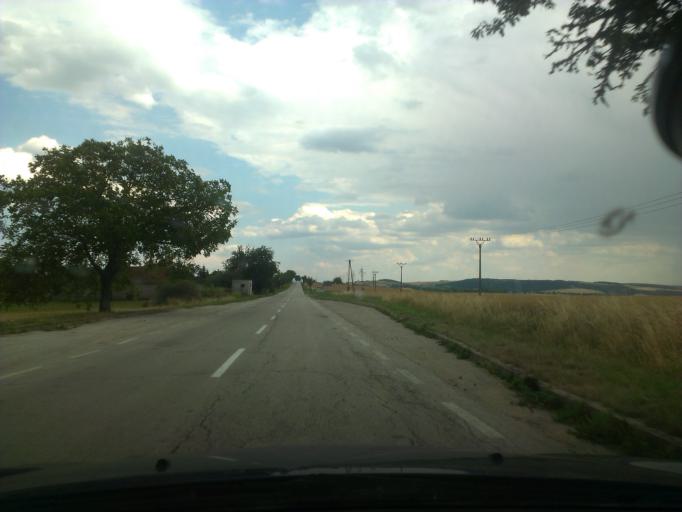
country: SK
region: Trenciansky
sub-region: Okres Myjava
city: Myjava
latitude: 48.7771
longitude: 17.5429
